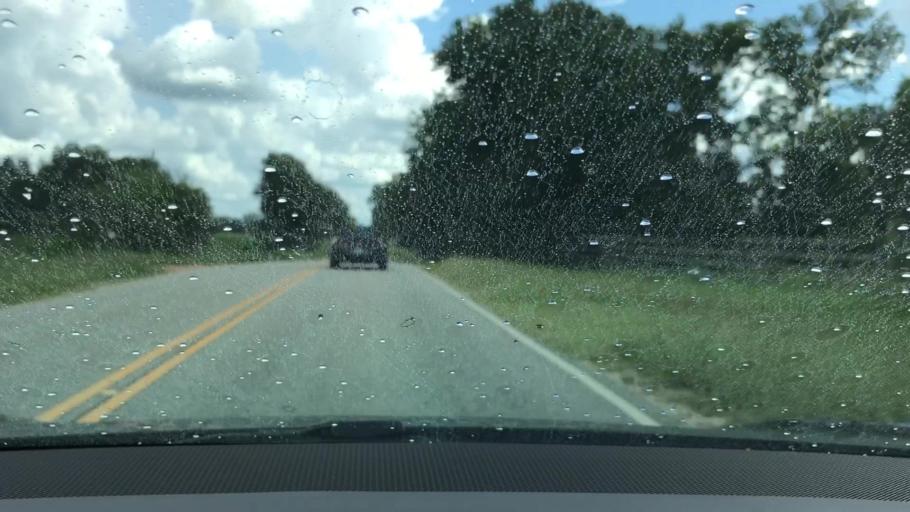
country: US
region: Alabama
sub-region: Montgomery County
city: Pike Road
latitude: 32.2444
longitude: -86.0933
